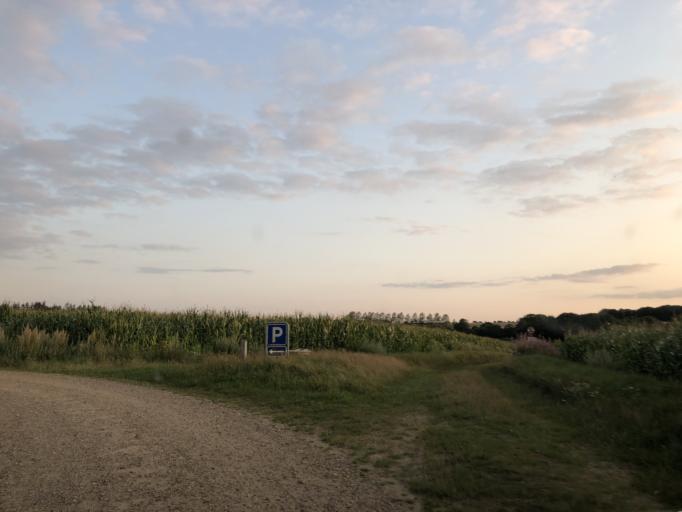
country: DK
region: Central Jutland
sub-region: Holstebro Kommune
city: Vinderup
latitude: 56.4575
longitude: 8.8924
